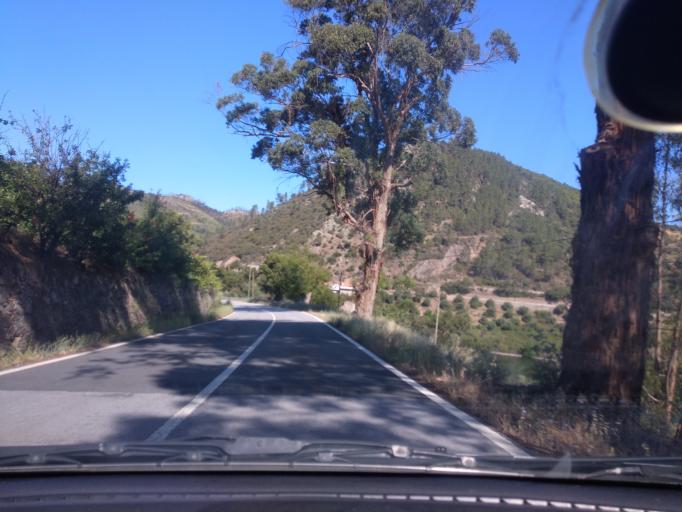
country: PT
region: Portalegre
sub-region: Nisa
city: Nisa
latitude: 39.6463
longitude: -7.6727
